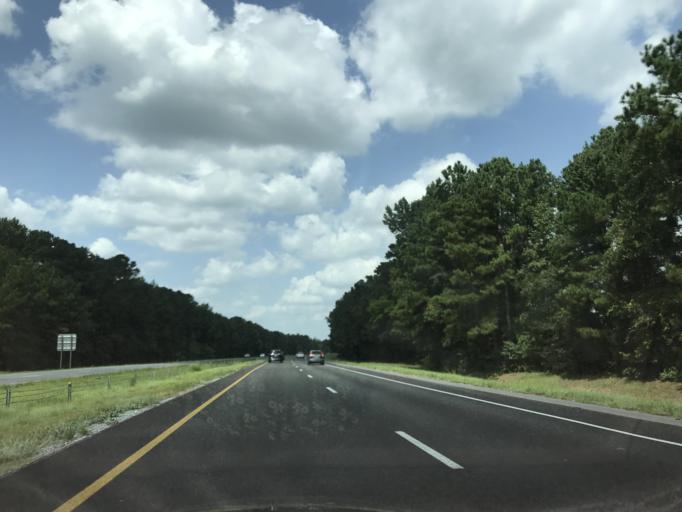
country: US
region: North Carolina
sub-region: Duplin County
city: Rose Hill
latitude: 34.7969
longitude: -77.9841
